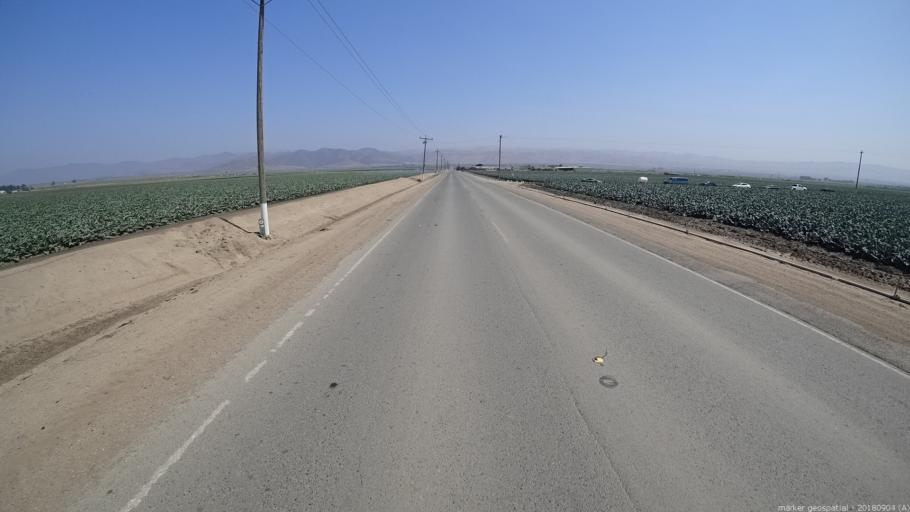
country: US
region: California
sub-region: Monterey County
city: Gonzales
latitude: 36.5328
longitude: -121.4691
